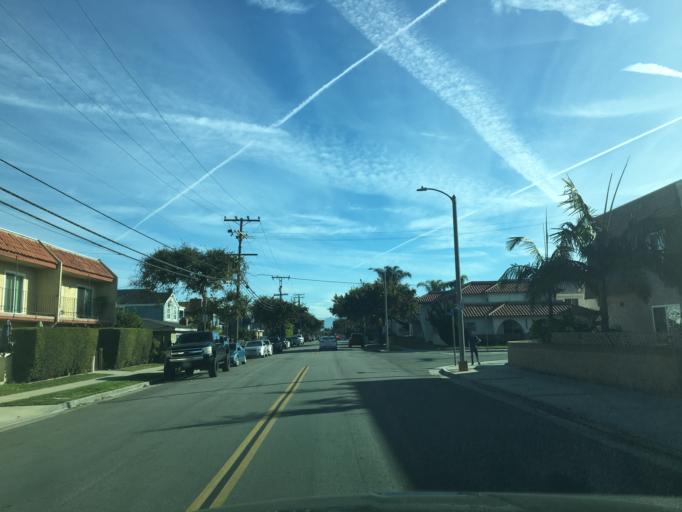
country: US
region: California
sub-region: Orange County
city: Westminster
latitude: 33.7190
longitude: -118.0452
